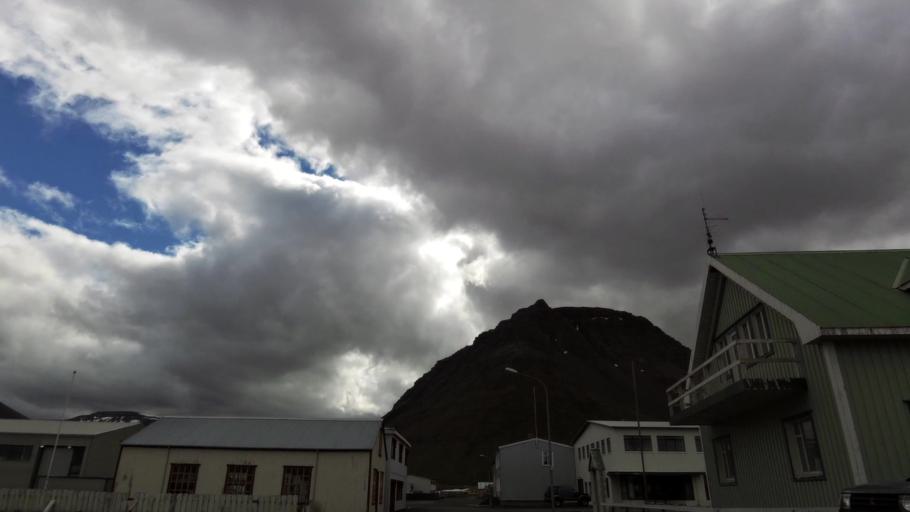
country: IS
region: Westfjords
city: Isafjoerdur
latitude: 66.1577
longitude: -23.2477
